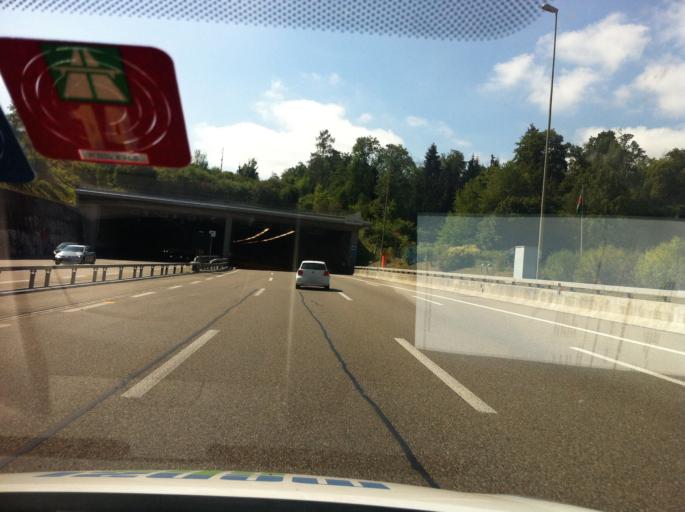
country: CH
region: Zurich
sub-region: Bezirk Zuerich
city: Zuerich (Kreis 2)
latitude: 47.3381
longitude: 8.5225
